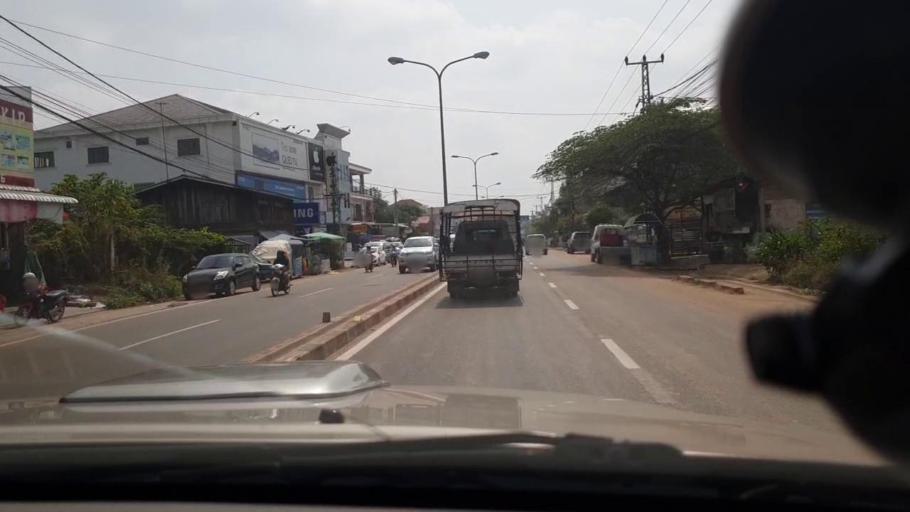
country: TH
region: Nong Khai
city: Si Chiang Mai
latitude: 17.9208
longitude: 102.6185
